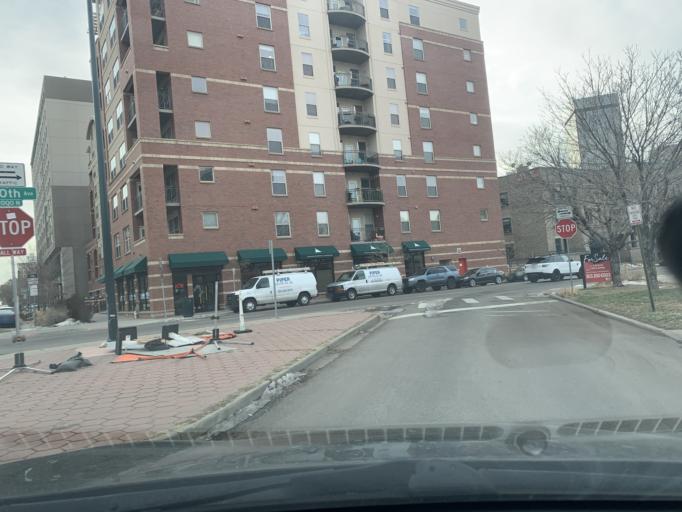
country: US
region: Colorado
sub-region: Denver County
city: Denver
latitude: 39.7478
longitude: -104.9837
